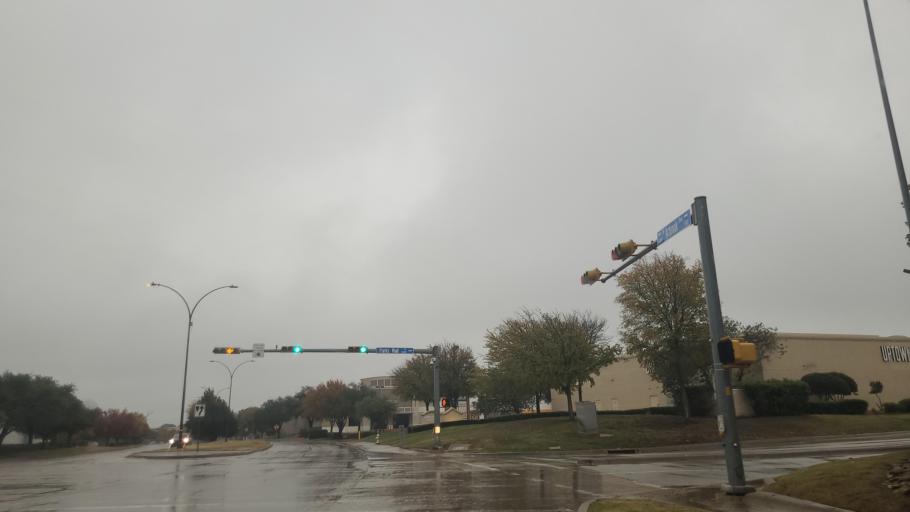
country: US
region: Texas
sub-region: Tarrant County
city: Dalworthington Gardens
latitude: 32.6820
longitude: -97.1268
